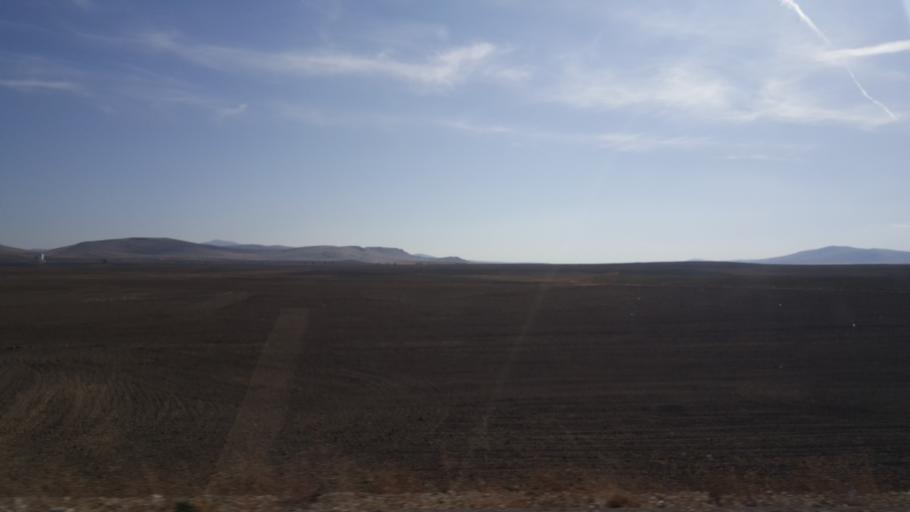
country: TR
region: Ankara
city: Yenice
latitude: 39.3811
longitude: 32.7858
